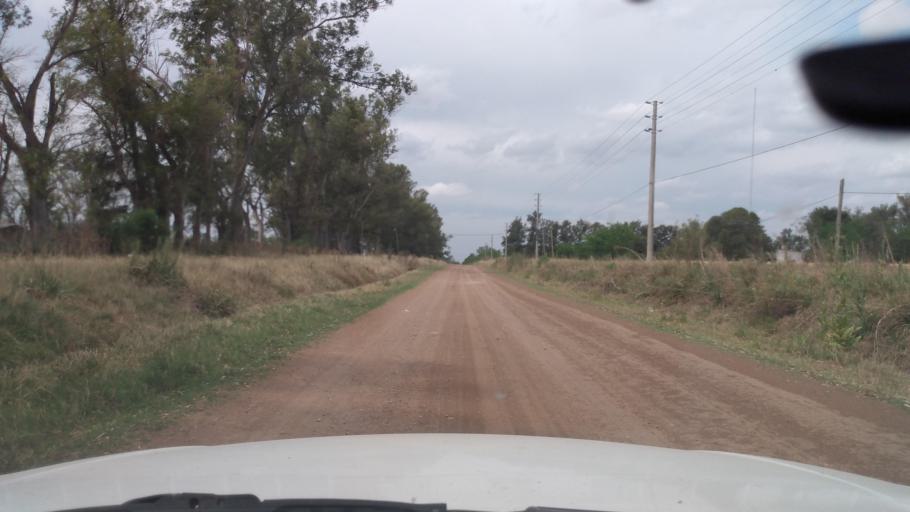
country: AR
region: Buenos Aires
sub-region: Partido de Lujan
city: Lujan
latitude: -34.5545
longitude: -59.1760
